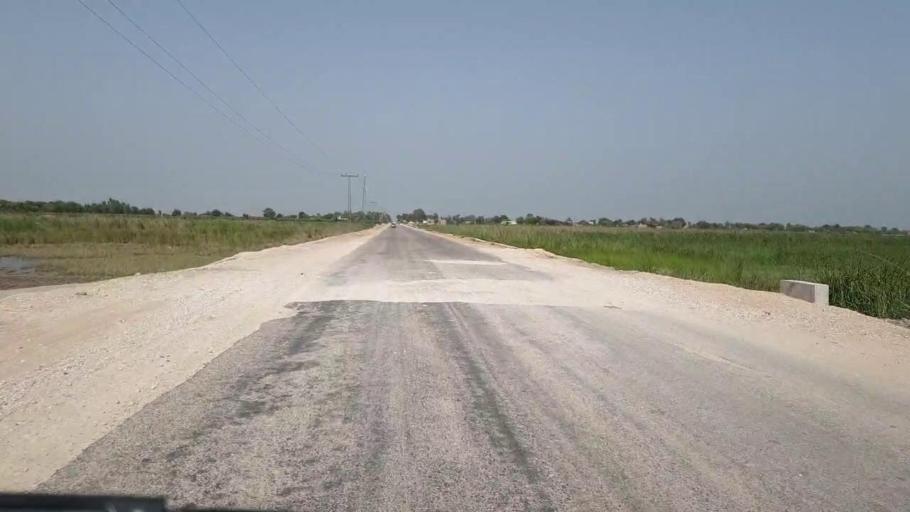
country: PK
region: Sindh
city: Sakrand
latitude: 26.2453
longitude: 68.2331
